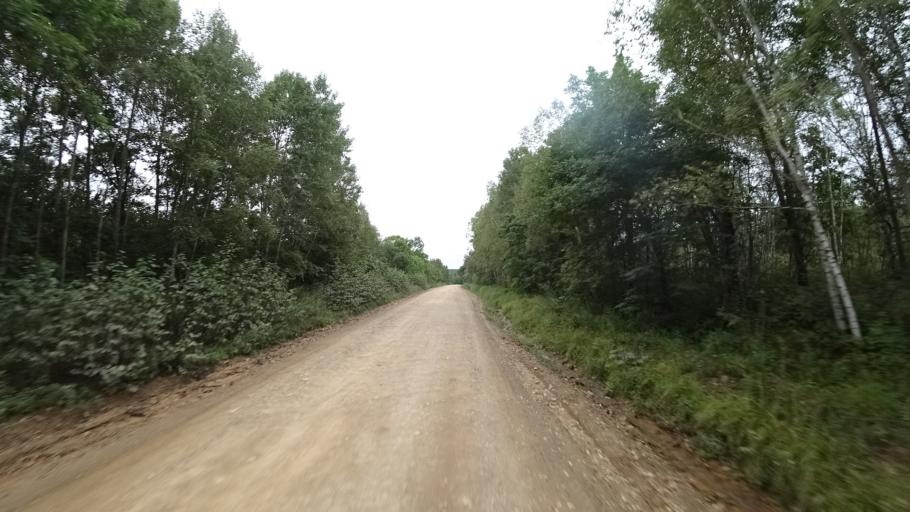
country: RU
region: Primorskiy
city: Rettikhovka
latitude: 44.1785
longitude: 132.8032
